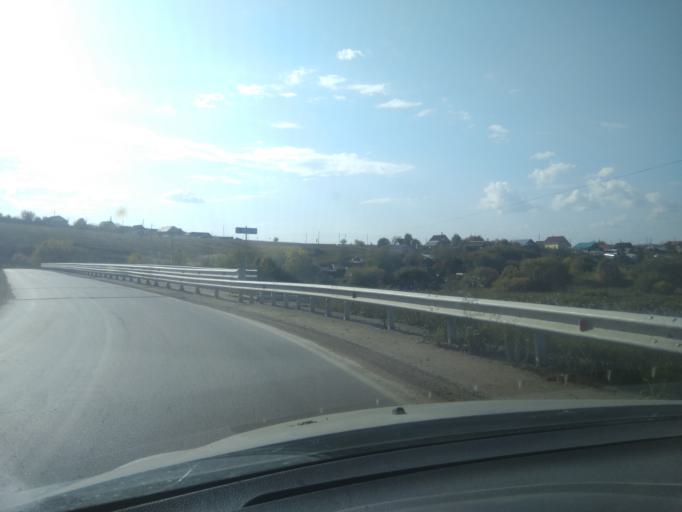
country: RU
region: Sverdlovsk
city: Pokrovskoye
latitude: 56.4366
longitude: 61.5933
